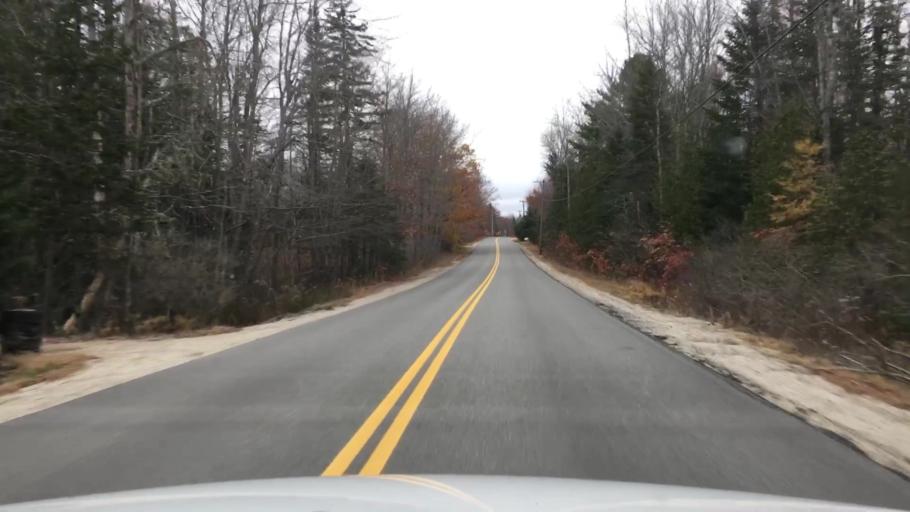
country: US
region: Maine
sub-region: Hancock County
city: Penobscot
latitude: 44.4602
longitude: -68.6376
